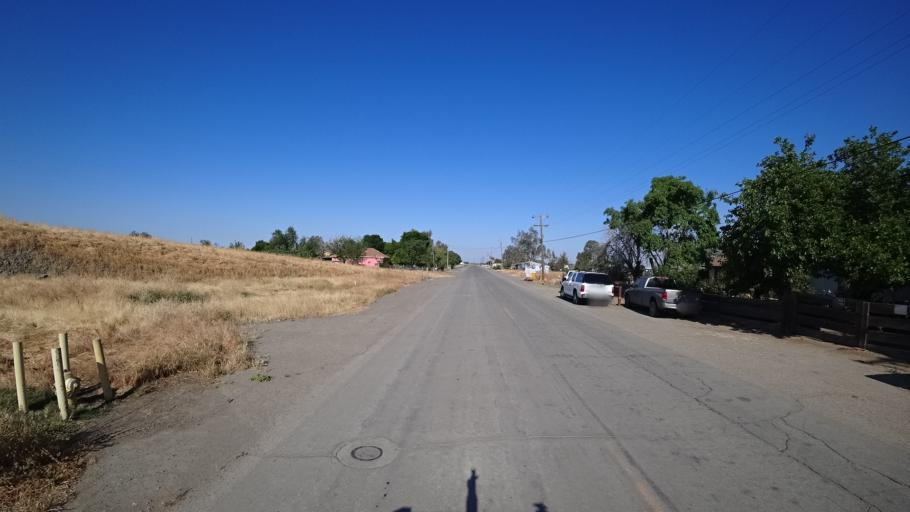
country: US
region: California
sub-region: Kings County
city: Corcoran
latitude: 36.1198
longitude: -119.5651
